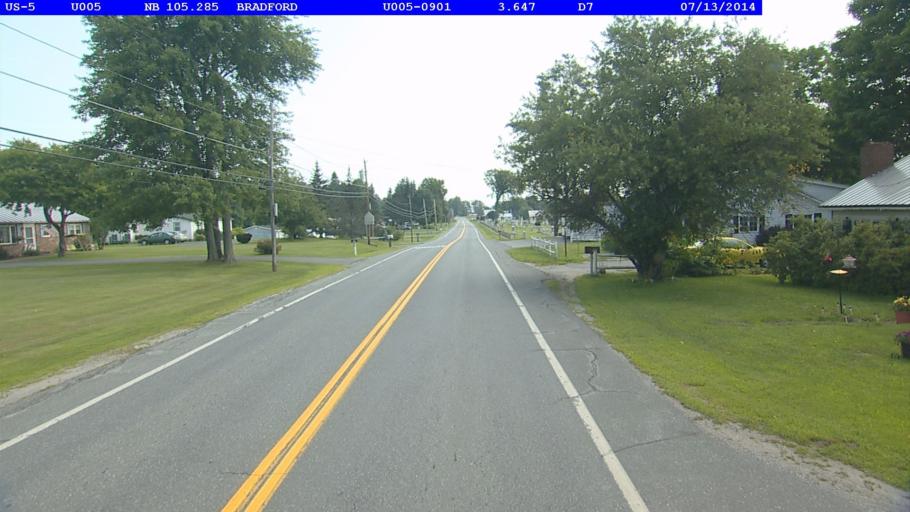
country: US
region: New Hampshire
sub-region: Grafton County
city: Haverhill
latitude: 44.0066
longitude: -72.1121
